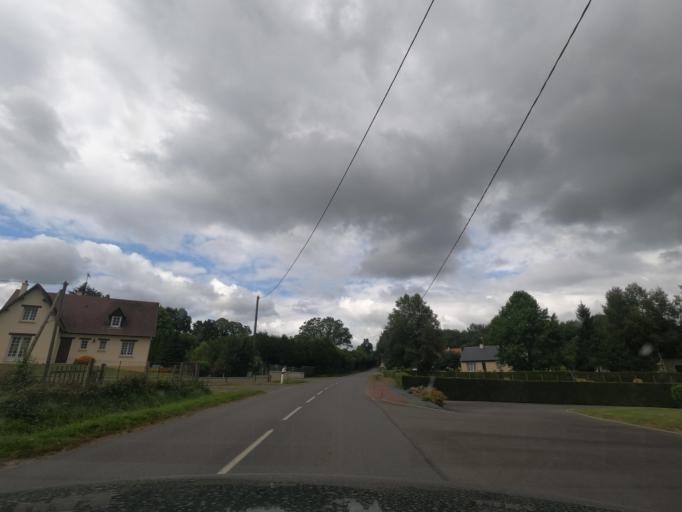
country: FR
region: Lower Normandy
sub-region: Departement de l'Orne
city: Briouze
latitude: 48.7084
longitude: -0.3639
